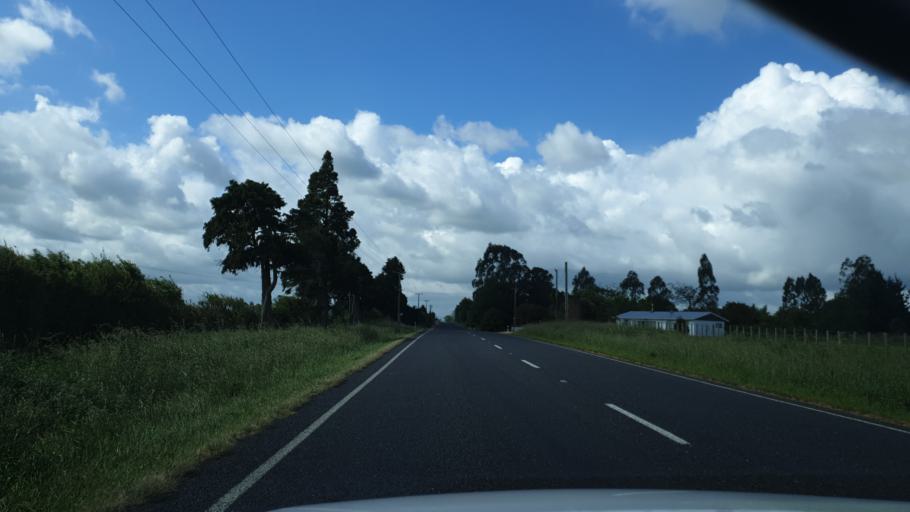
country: NZ
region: Waikato
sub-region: Hauraki District
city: Paeroa
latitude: -37.5089
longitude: 175.4957
